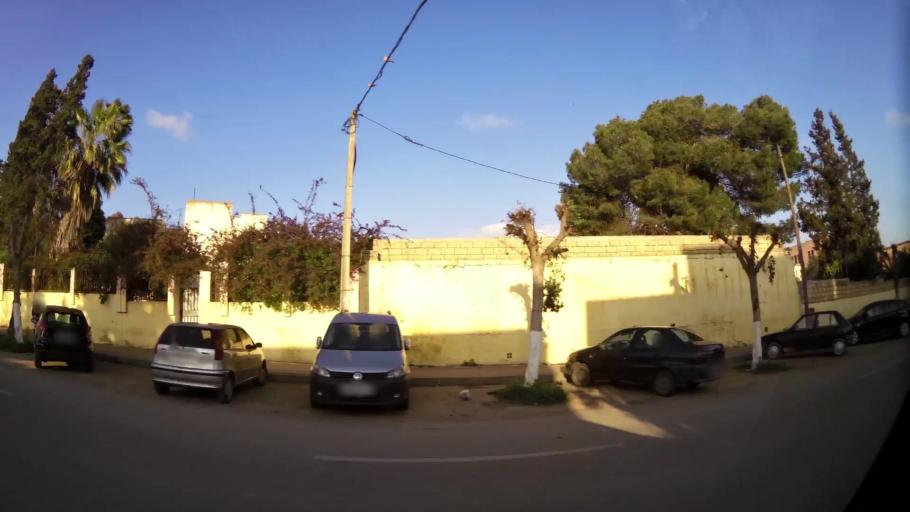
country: MA
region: Chaouia-Ouardigha
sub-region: Settat Province
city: Settat
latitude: 33.0046
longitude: -7.6159
